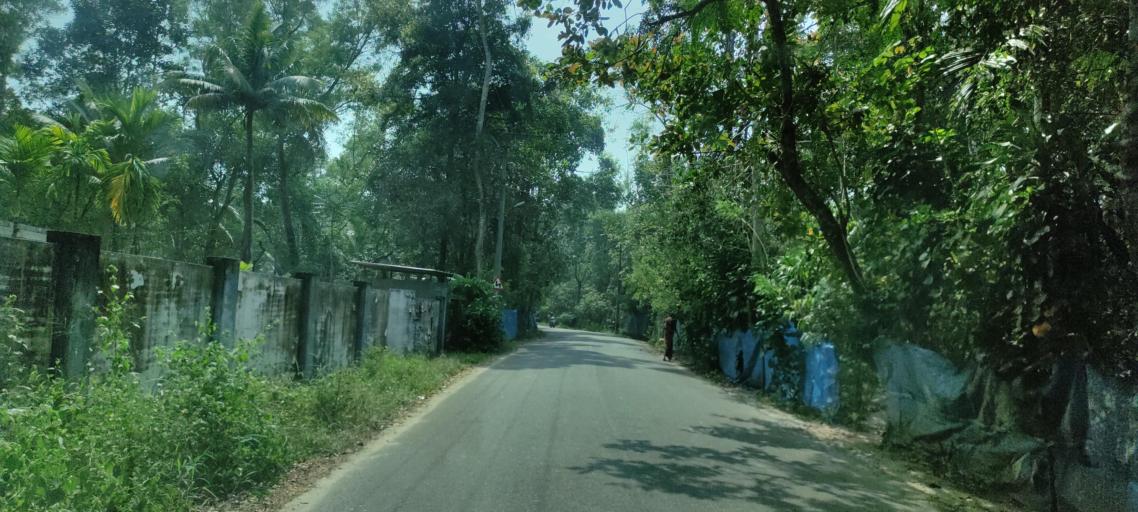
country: IN
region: Kerala
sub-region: Alappuzha
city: Shertallai
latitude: 9.6255
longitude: 76.3502
